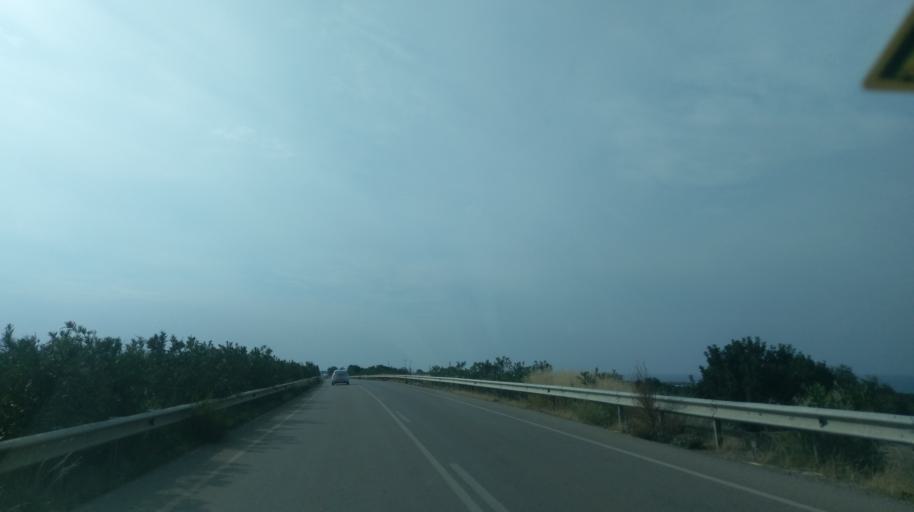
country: CY
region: Ammochostos
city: Lefkonoiko
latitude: 35.4058
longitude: 33.7734
